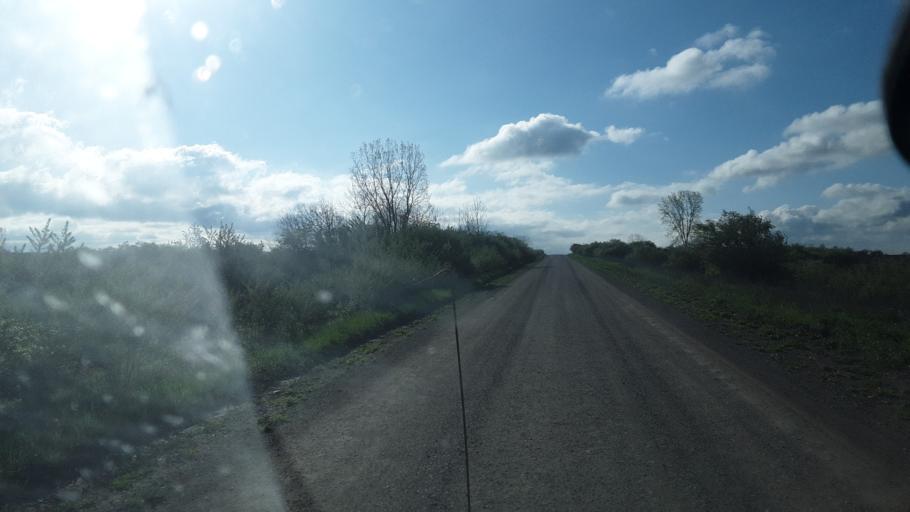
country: US
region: Ohio
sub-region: Noble County
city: Caldwell
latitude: 39.8090
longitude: -81.6546
